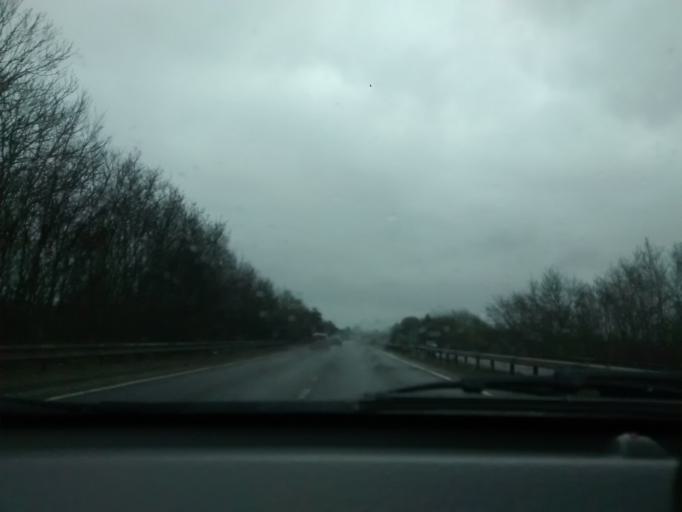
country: GB
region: England
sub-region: Suffolk
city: Stowmarket
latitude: 52.1975
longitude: 0.9961
